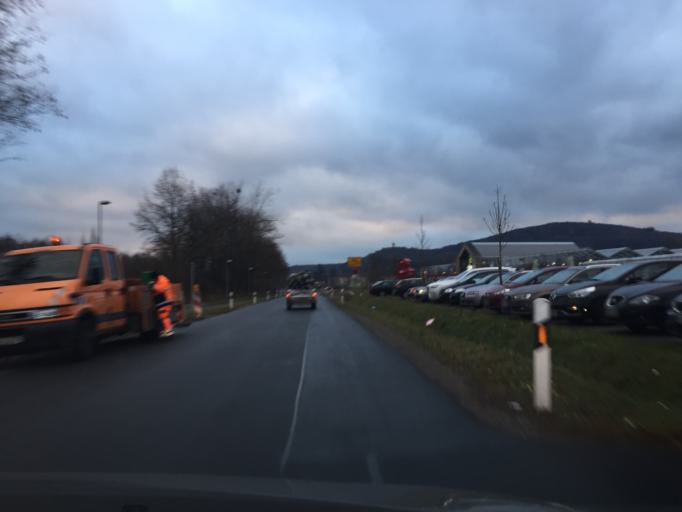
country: DE
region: Bavaria
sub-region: Regierungsbezirk Unterfranken
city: Goldbach
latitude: 49.9888
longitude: 9.1686
